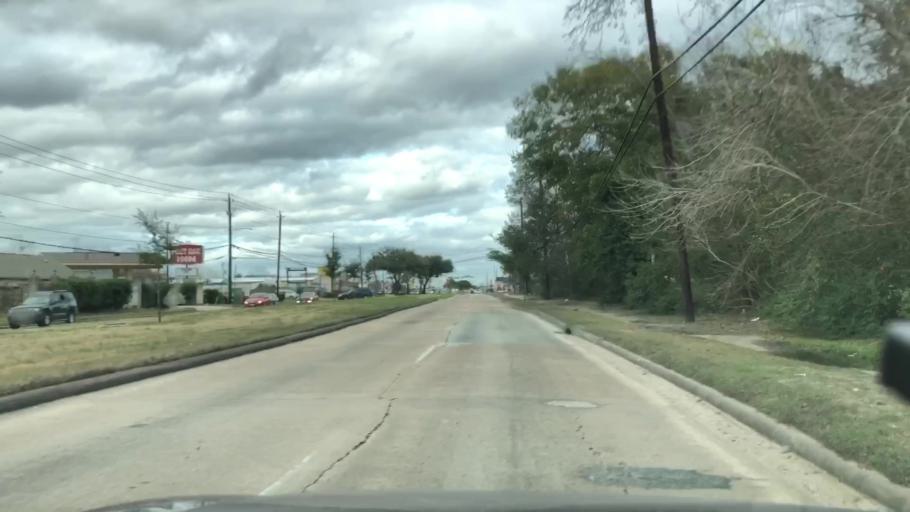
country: US
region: Texas
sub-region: Fort Bend County
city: Missouri City
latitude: 29.6128
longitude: -95.4648
